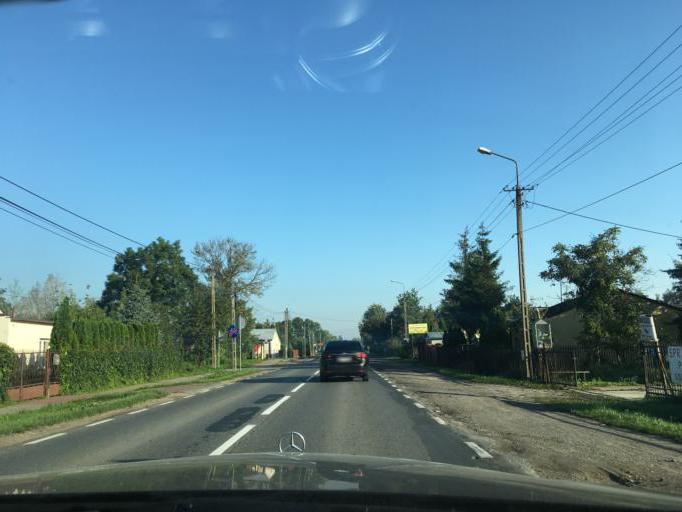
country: PL
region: Masovian Voivodeship
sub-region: Powiat grodziski
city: Grodzisk Mazowiecki
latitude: 52.1337
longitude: 20.6177
